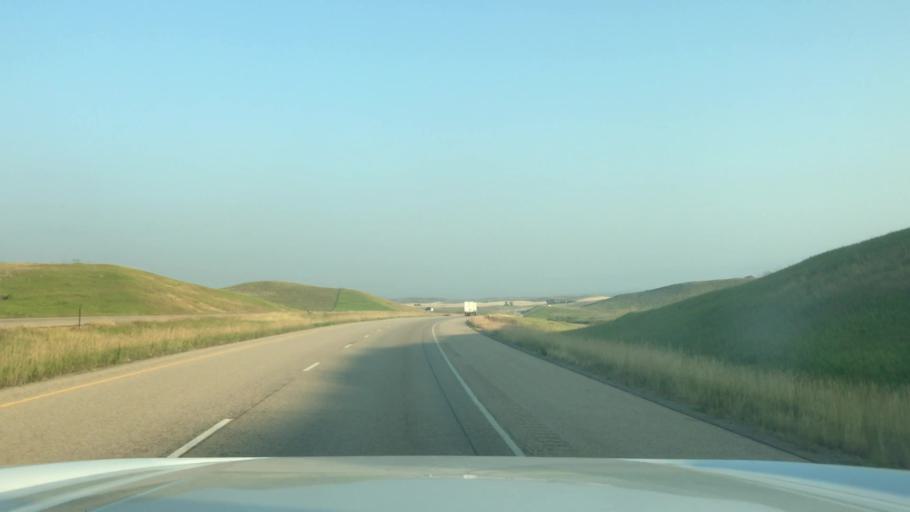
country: US
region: Wyoming
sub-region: Sheridan County
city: Sheridan
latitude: 45.0254
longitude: -107.3142
